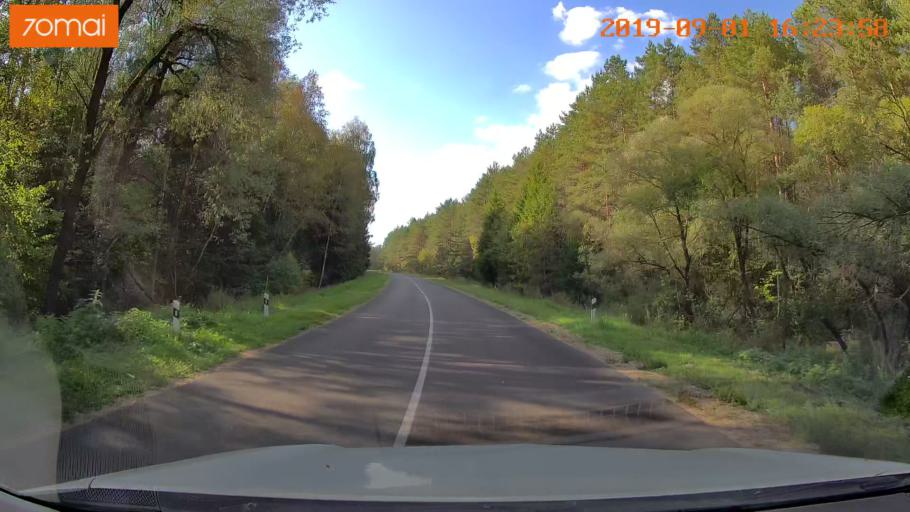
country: RU
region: Kaluga
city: Maloyaroslavets
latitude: 54.8860
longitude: 36.5287
